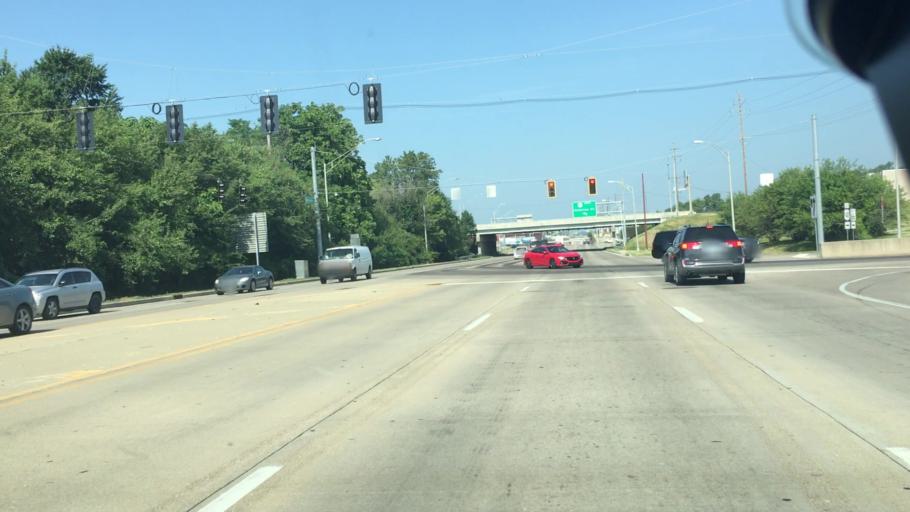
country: US
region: Indiana
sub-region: Vanderburgh County
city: Evansville
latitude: 37.9990
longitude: -87.5354
